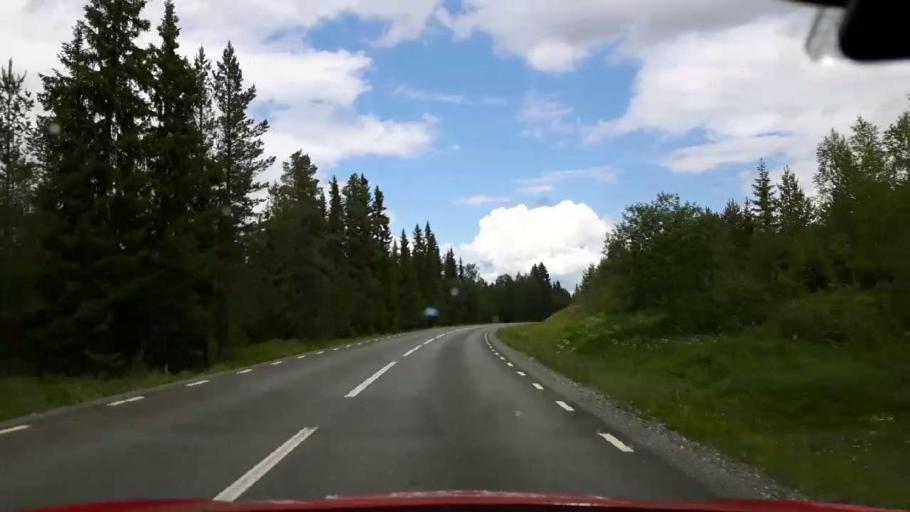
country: SE
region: Jaemtland
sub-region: Krokoms Kommun
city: Krokom
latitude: 63.5910
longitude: 14.2969
